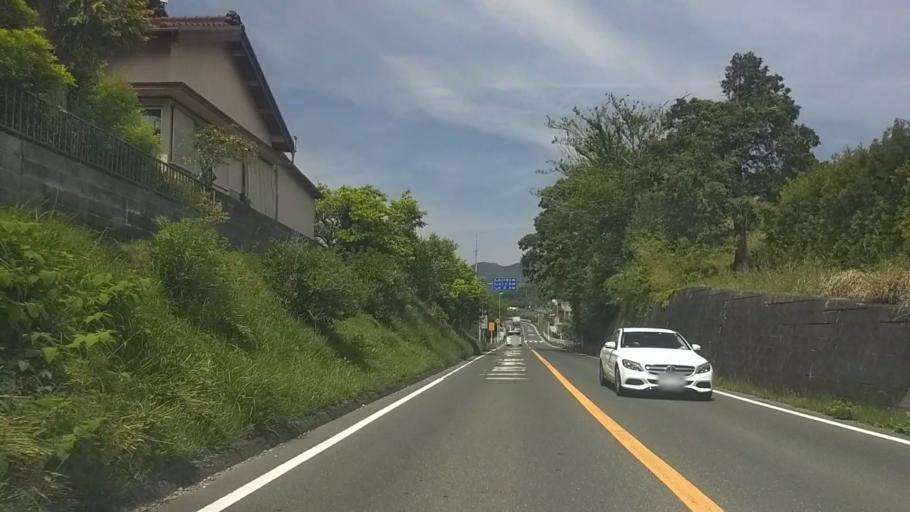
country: JP
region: Shizuoka
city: Kosai-shi
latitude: 34.7882
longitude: 137.5821
